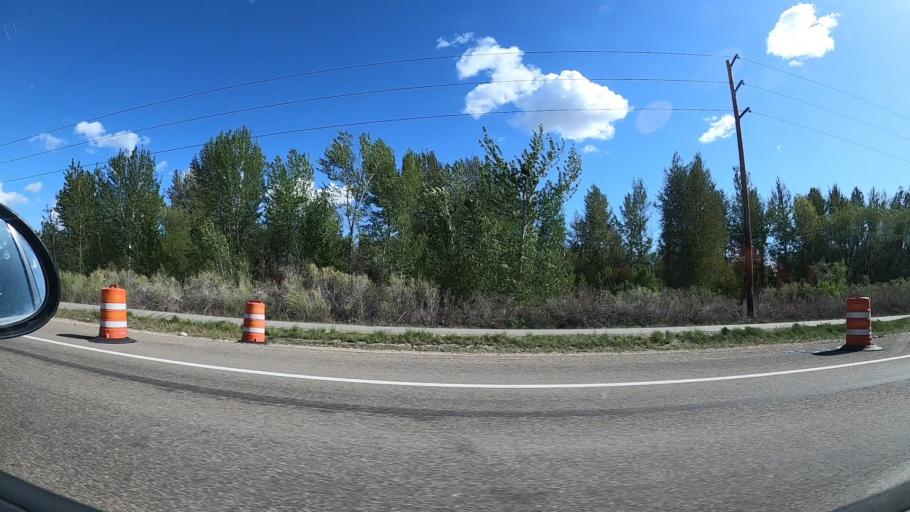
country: US
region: Idaho
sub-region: Ada County
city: Eagle
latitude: 43.6921
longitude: -116.3659
